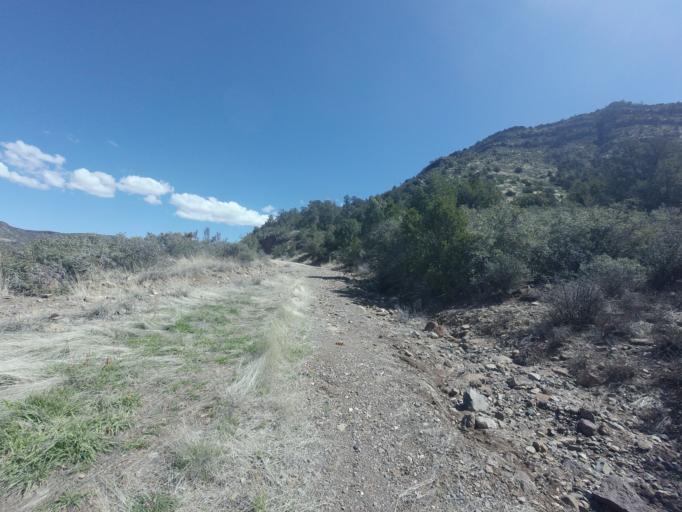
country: US
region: Arizona
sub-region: Gila County
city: Pine
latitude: 34.4001
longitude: -111.6111
